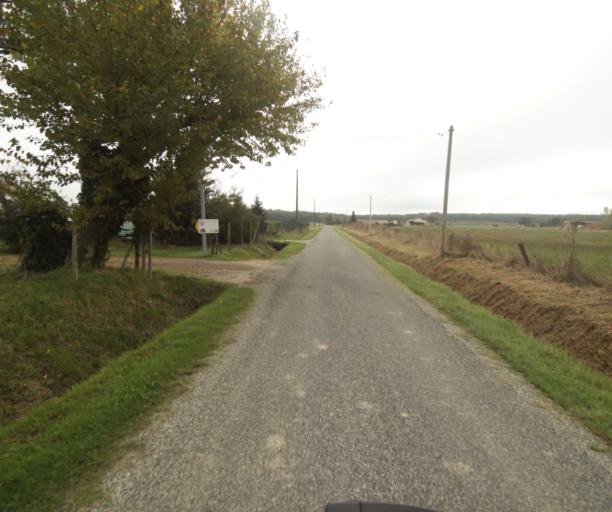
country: FR
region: Midi-Pyrenees
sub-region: Departement du Tarn-et-Garonne
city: Campsas
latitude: 43.8801
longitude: 1.3583
